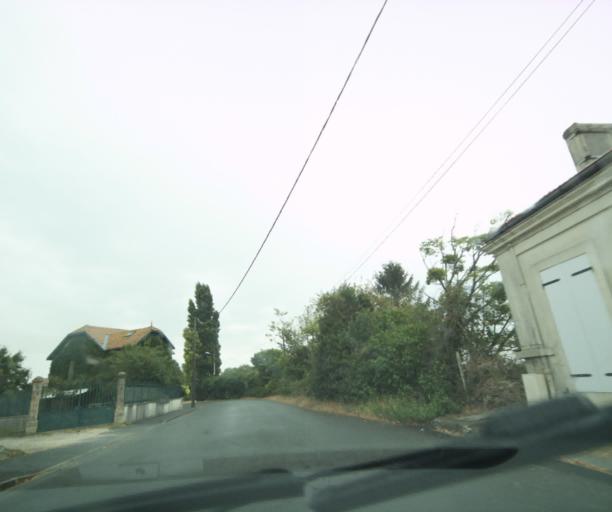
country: FR
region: Poitou-Charentes
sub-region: Departement de la Charente-Maritime
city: Tonnay-Charente
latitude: 45.9438
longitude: -0.9052
